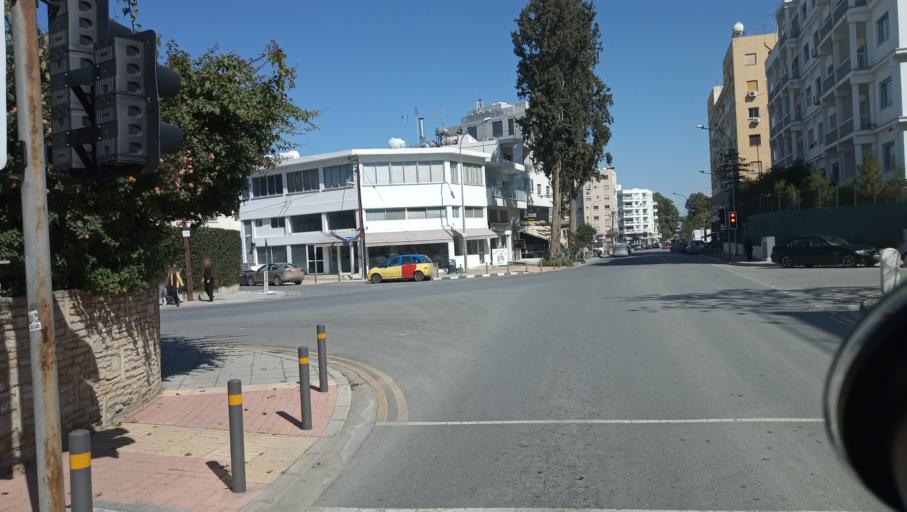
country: CY
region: Lefkosia
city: Nicosia
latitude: 35.1687
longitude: 33.3474
